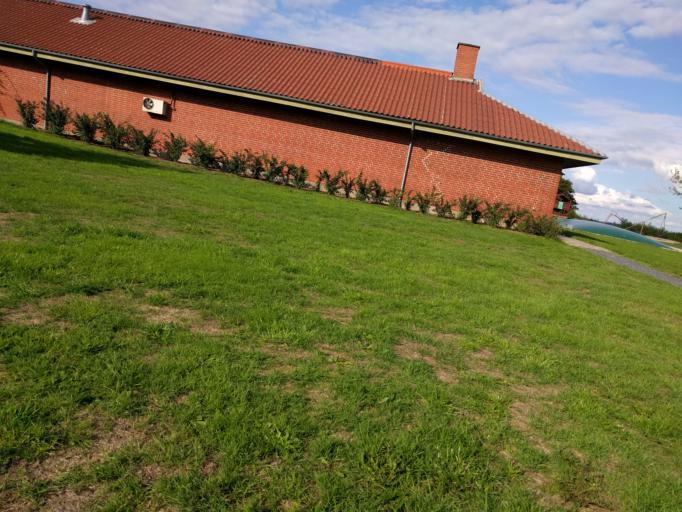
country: DK
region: Central Jutland
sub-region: Skive Kommune
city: Hojslev
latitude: 56.6038
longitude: 9.2847
